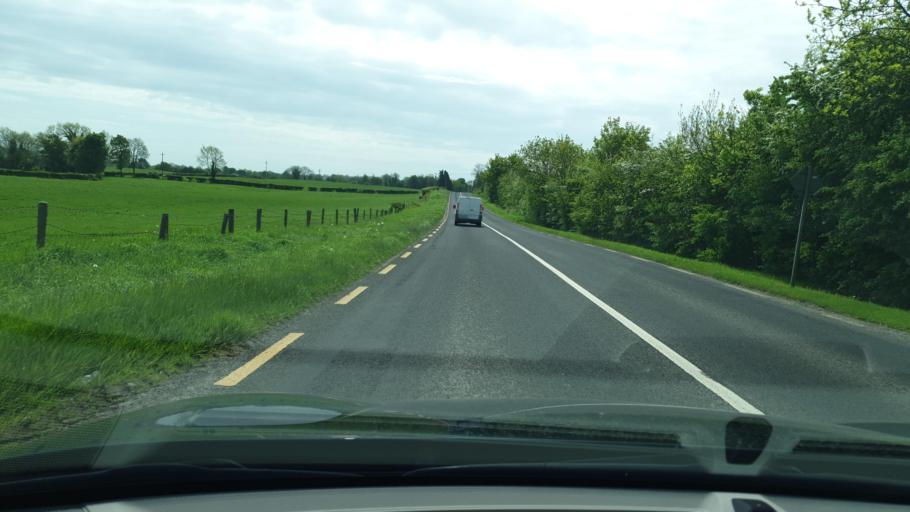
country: IE
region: Leinster
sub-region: An Mhi
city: Navan
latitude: 53.7574
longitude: -6.7239
